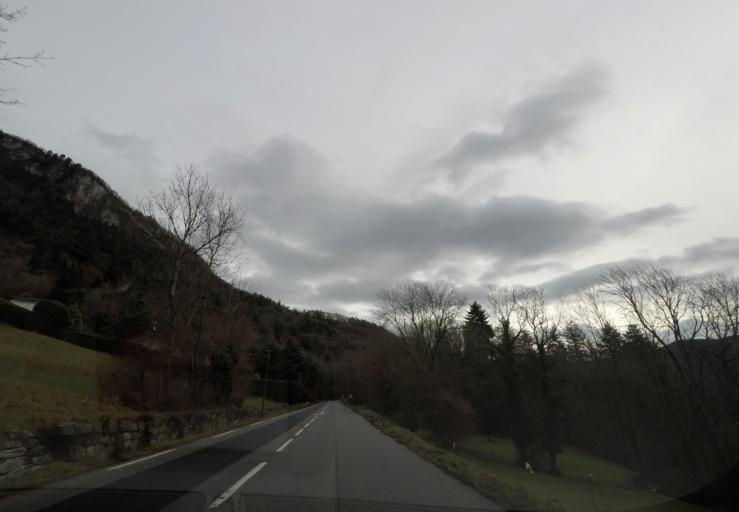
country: FR
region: Rhone-Alpes
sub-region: Departement de la Haute-Savoie
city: Thyez
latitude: 46.0882
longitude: 6.5494
